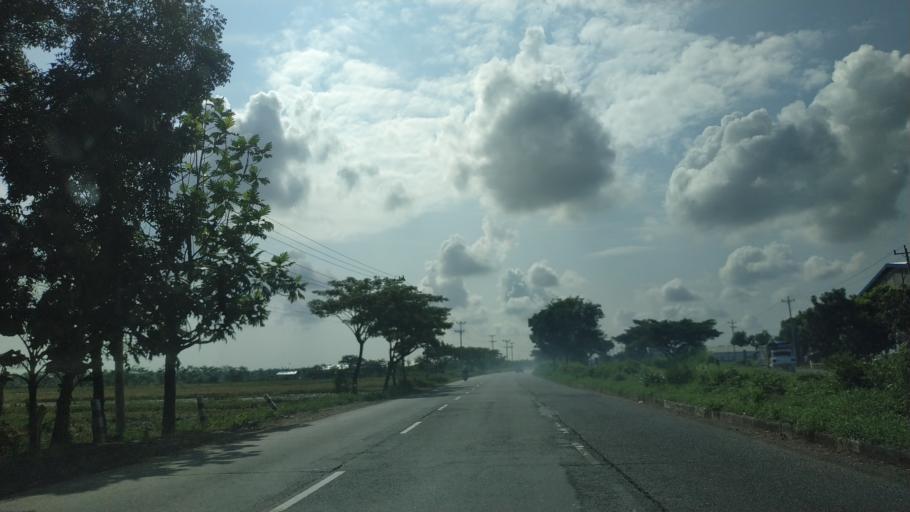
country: ID
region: Central Java
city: Comal
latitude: -6.9005
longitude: 109.5070
